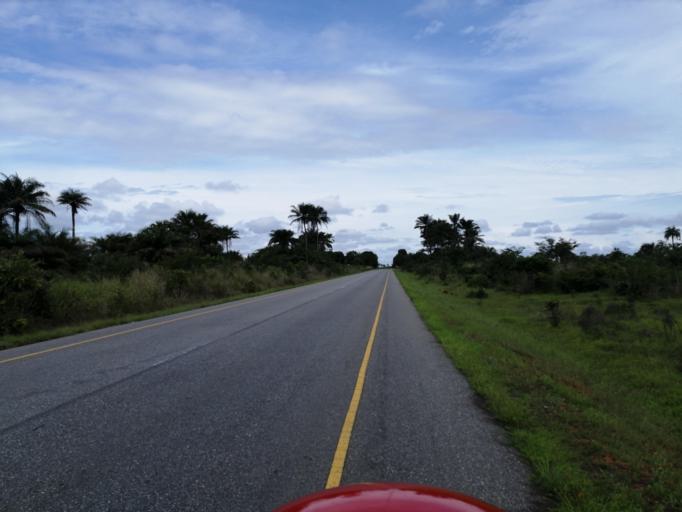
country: SL
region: Northern Province
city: Port Loko
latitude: 8.7386
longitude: -12.9440
